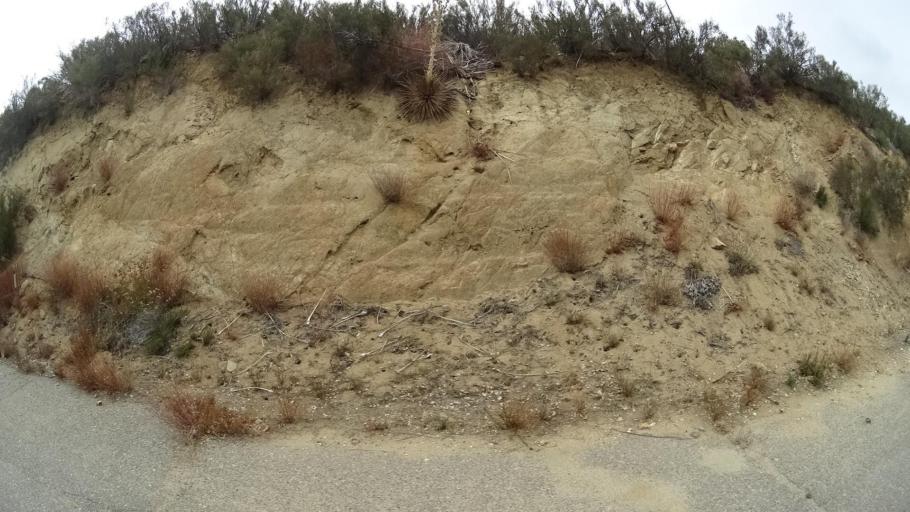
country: US
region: California
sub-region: San Diego County
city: San Diego Country Estates
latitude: 32.9686
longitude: -116.6697
